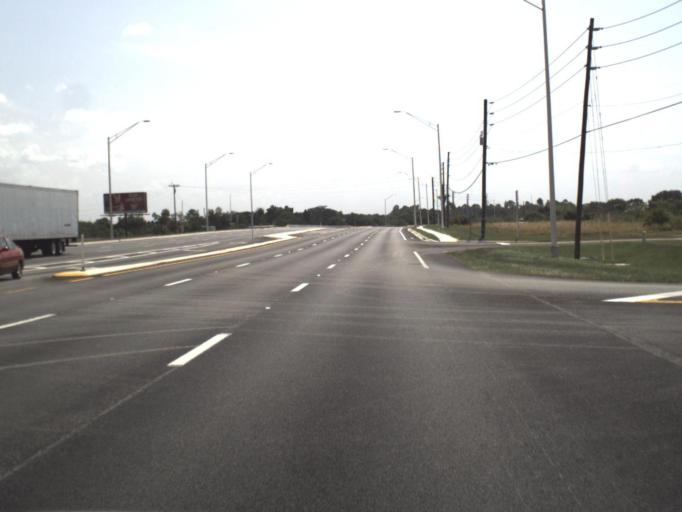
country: US
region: Florida
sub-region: Highlands County
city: Avon Park
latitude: 27.6342
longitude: -81.5190
